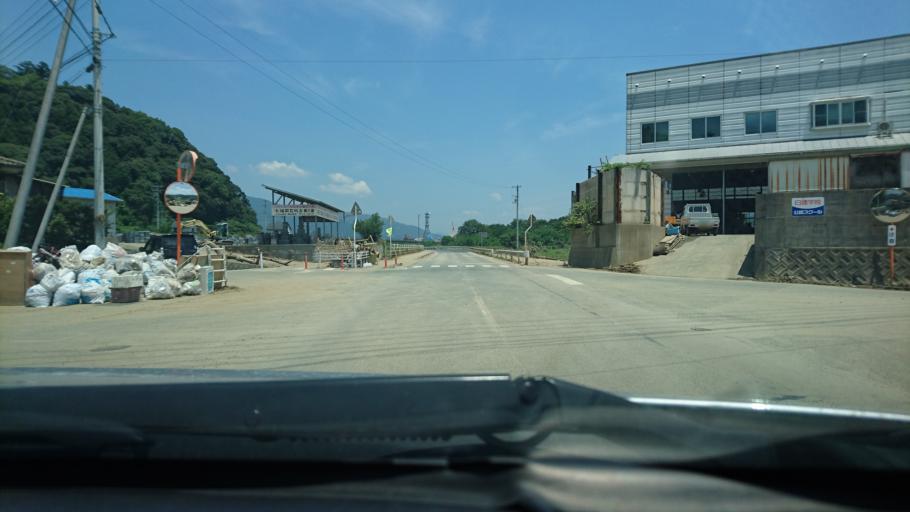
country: JP
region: Ehime
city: Ozu
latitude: 33.5123
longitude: 132.5368
